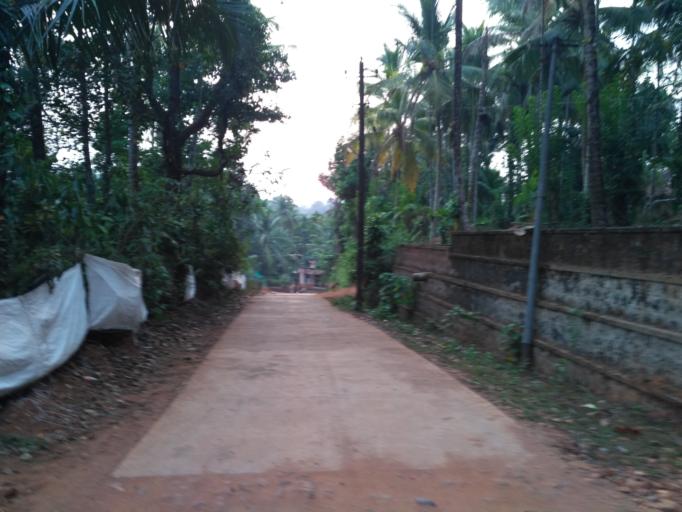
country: IN
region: Karnataka
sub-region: Kodagu
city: Somvarpet
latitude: 12.6617
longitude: 75.6183
